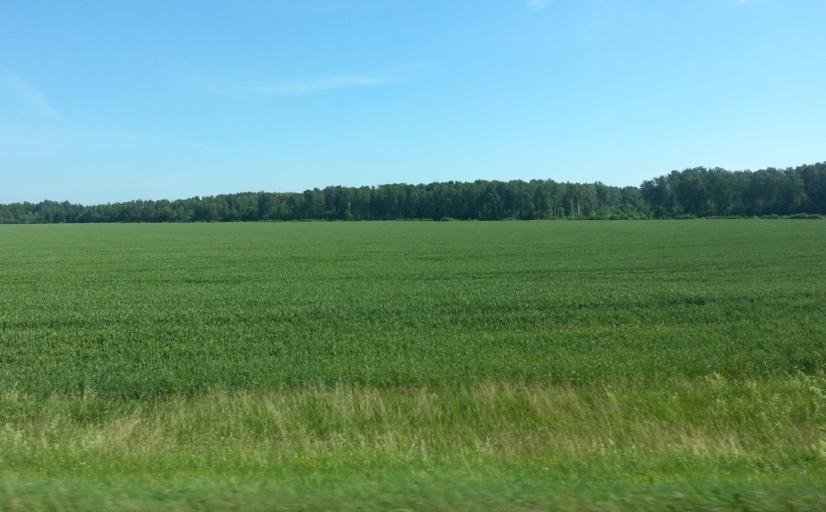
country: LT
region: Panevezys
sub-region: Panevezys City
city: Panevezys
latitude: 55.6848
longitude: 24.2874
